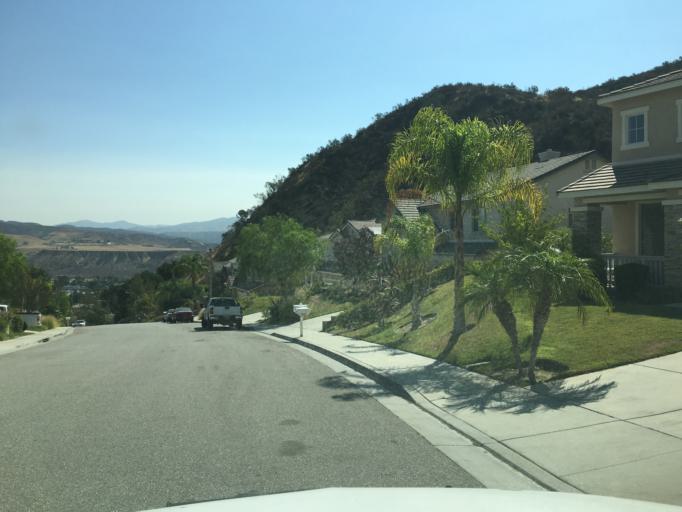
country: US
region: California
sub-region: Los Angeles County
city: Castaic
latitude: 34.4844
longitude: -118.6278
